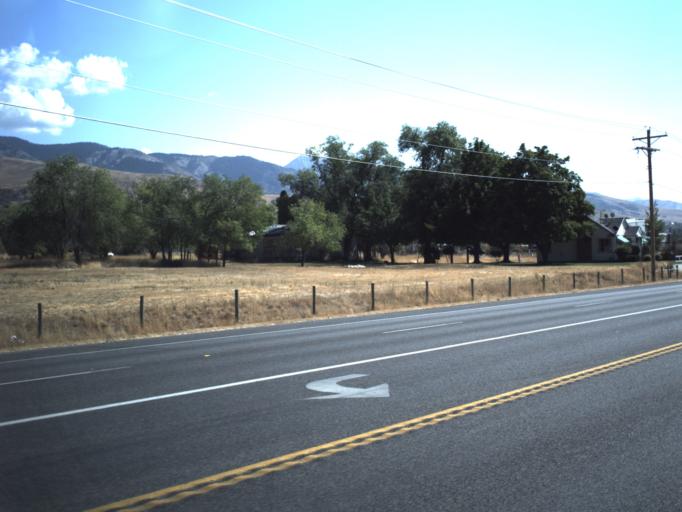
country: US
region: Utah
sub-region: Cache County
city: Richmond
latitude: 41.9427
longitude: -111.8139
